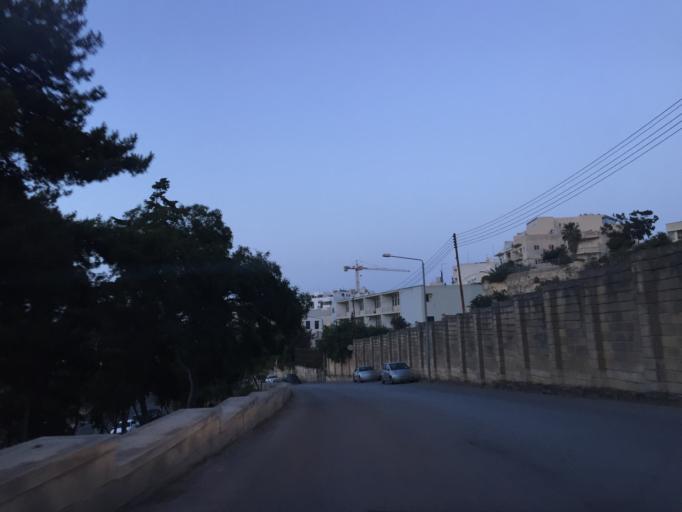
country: MT
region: Saint Julian
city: San Giljan
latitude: 35.9158
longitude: 14.4870
